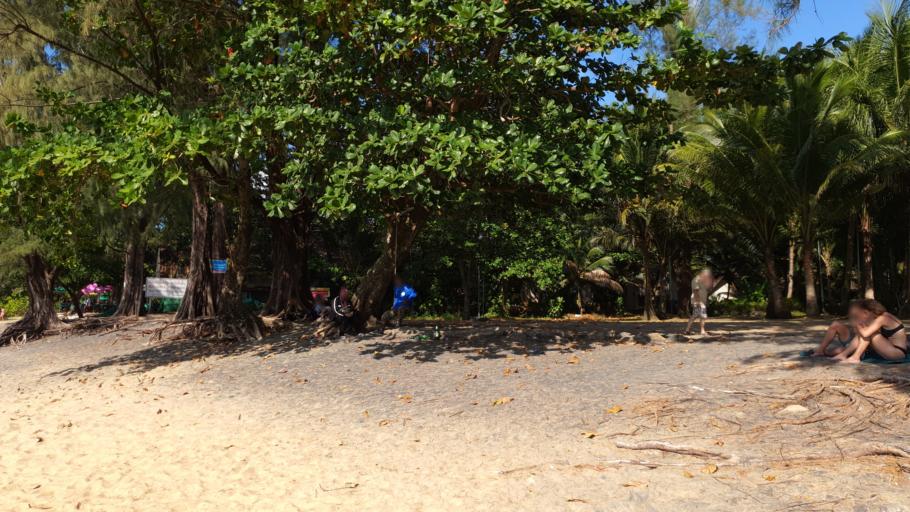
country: TH
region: Phangnga
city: Ban Khao Lak
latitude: 8.6453
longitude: 98.2463
